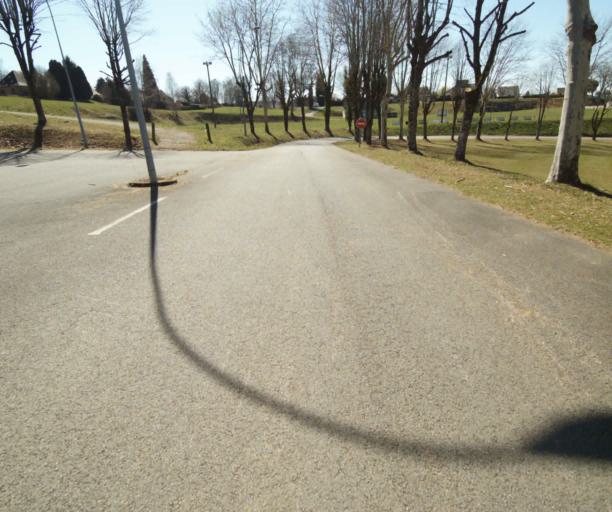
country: FR
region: Limousin
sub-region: Departement de la Correze
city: Seilhac
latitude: 45.3763
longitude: 1.6997
